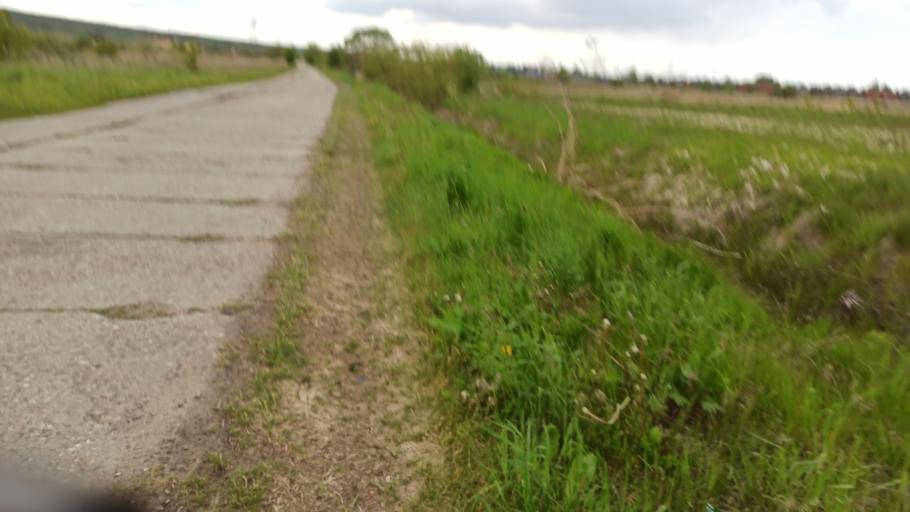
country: PL
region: Swietokrzyskie
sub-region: Powiat skarzyski
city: Skarzysko Koscielne
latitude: 51.1387
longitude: 20.9031
